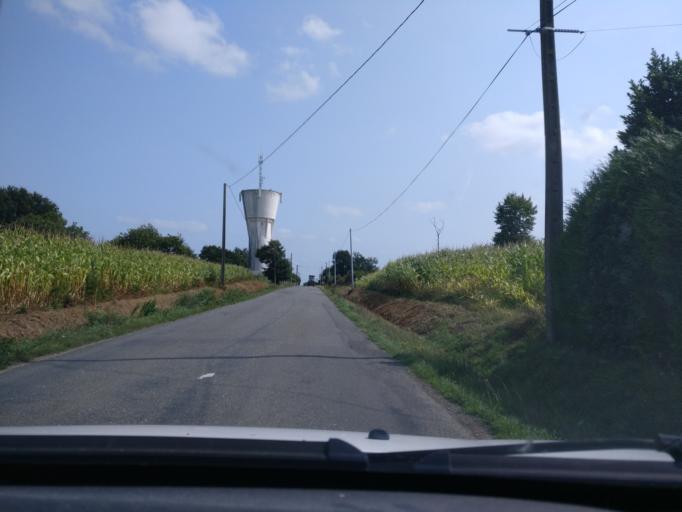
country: FR
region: Brittany
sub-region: Departement d'Ille-et-Vilaine
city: Gosne
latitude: 48.2510
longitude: -1.4756
